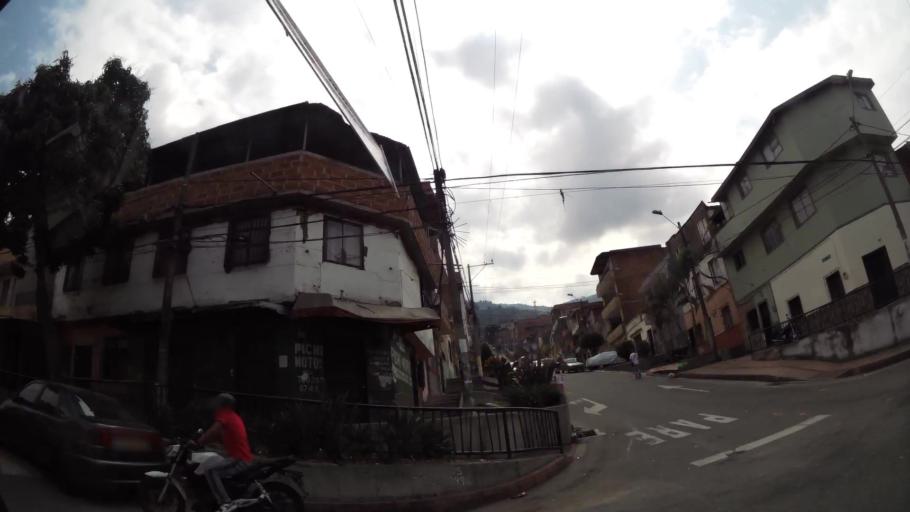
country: CO
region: Antioquia
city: Medellin
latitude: 6.2743
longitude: -75.5528
